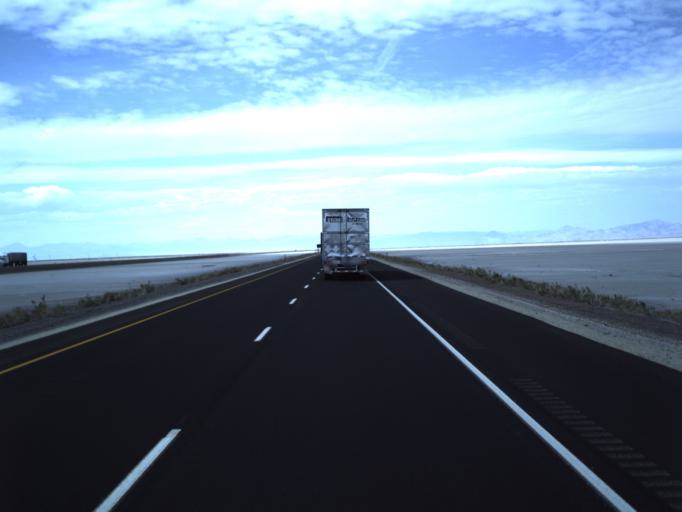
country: US
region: Utah
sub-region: Tooele County
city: Wendover
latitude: 40.7332
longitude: -113.5597
